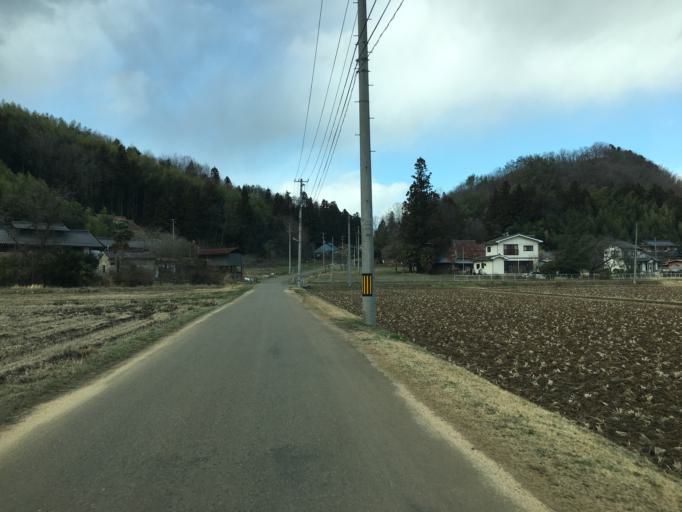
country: JP
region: Fukushima
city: Yanagawamachi-saiwaicho
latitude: 37.8316
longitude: 140.6110
